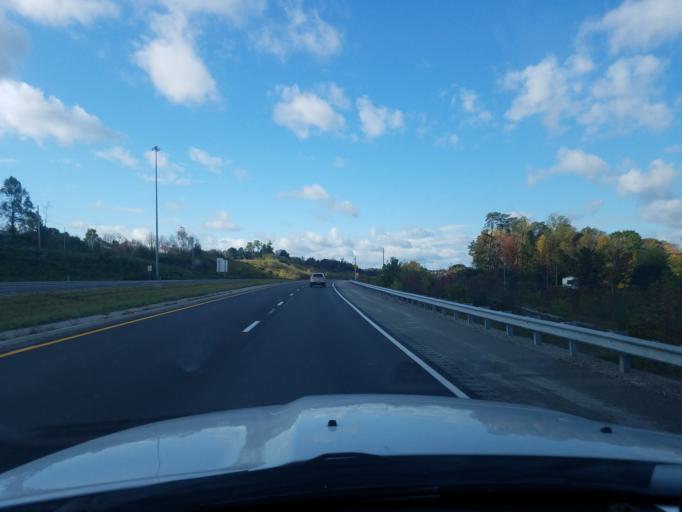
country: US
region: Kentucky
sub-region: Pulaski County
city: Somerset
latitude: 37.1032
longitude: -84.6649
